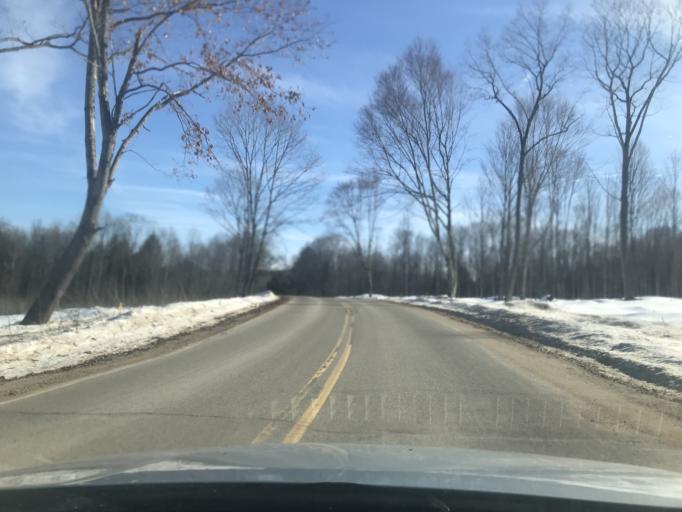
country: US
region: Michigan
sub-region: Dickinson County
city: Kingsford
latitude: 45.4039
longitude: -88.3778
